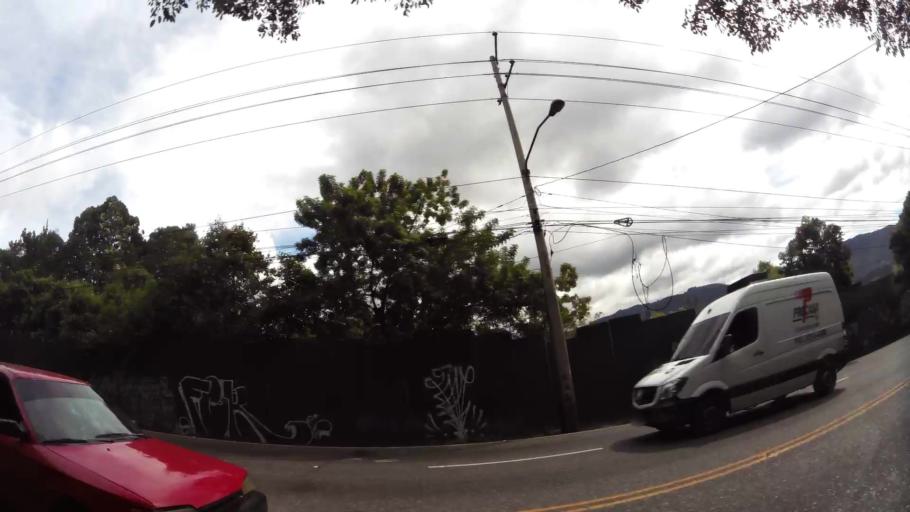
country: GT
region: Guatemala
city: Santa Catarina Pinula
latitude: 14.5692
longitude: -90.5277
